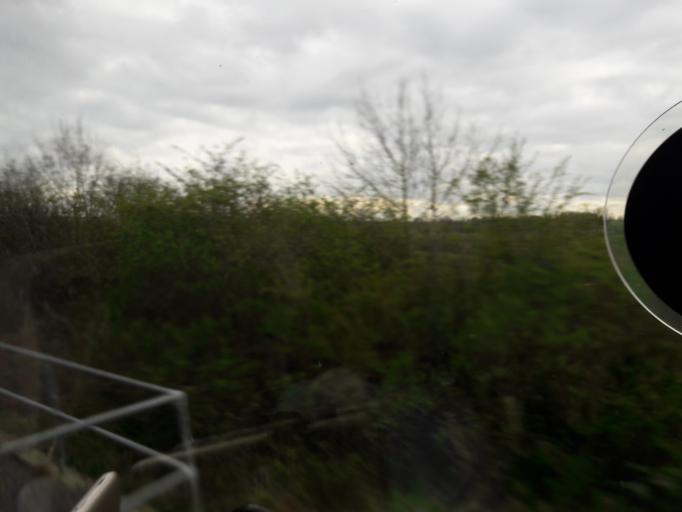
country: IE
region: Leinster
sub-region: An Longfort
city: Granard
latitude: 53.6692
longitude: -7.4963
